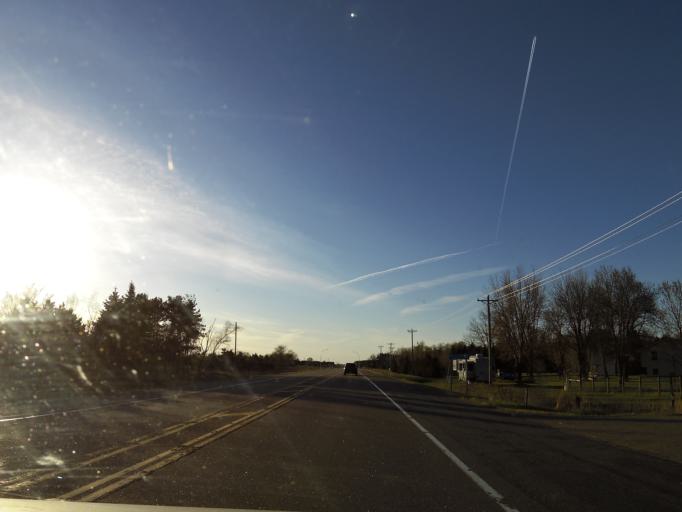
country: US
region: Wisconsin
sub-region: Pierce County
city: Prescott
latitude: 44.6709
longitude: -92.7869
